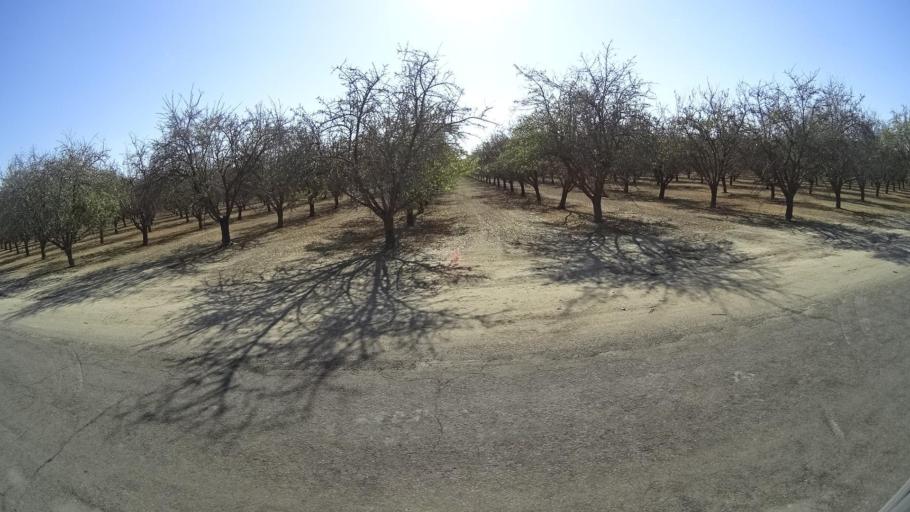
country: US
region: California
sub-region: Kern County
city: McFarland
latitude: 35.7035
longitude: -119.1448
